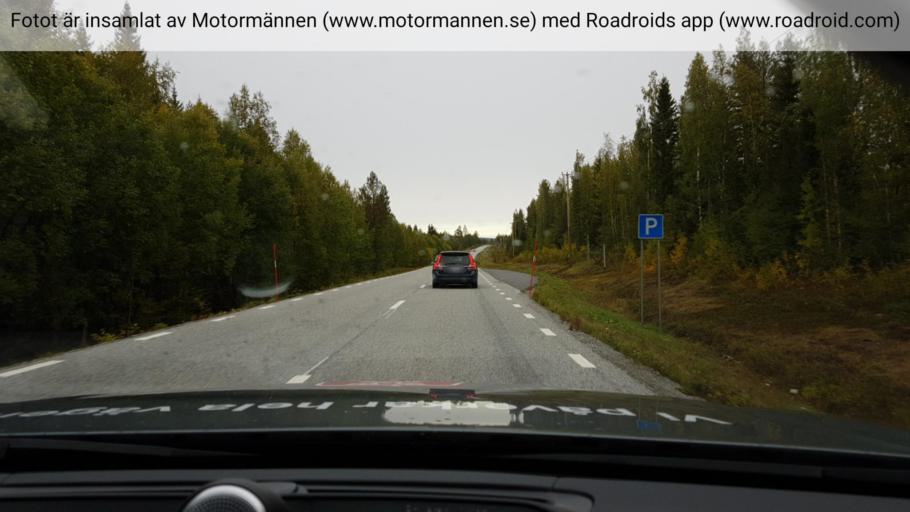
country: SE
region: Jaemtland
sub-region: Stroemsunds Kommun
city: Stroemsund
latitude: 63.9673
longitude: 15.4847
